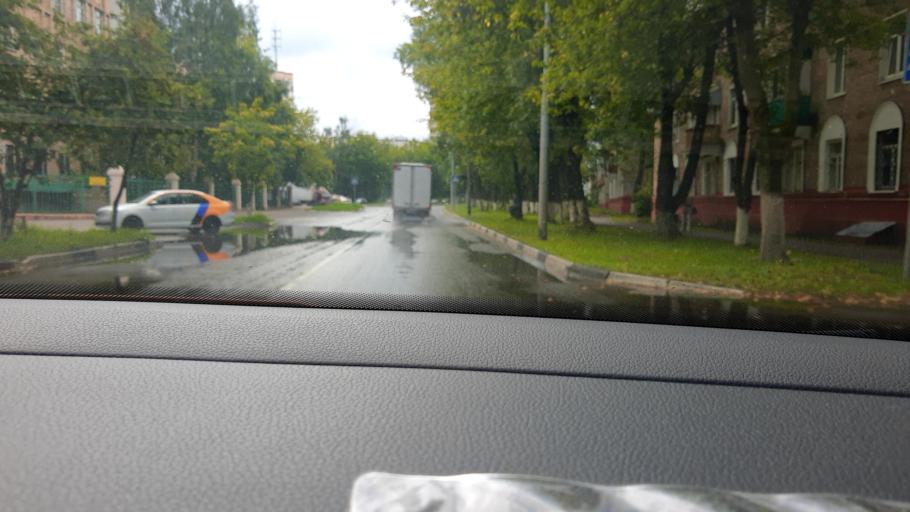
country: RU
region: Moskovskaya
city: Zheleznodorozhnyy
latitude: 55.7489
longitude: 37.9987
